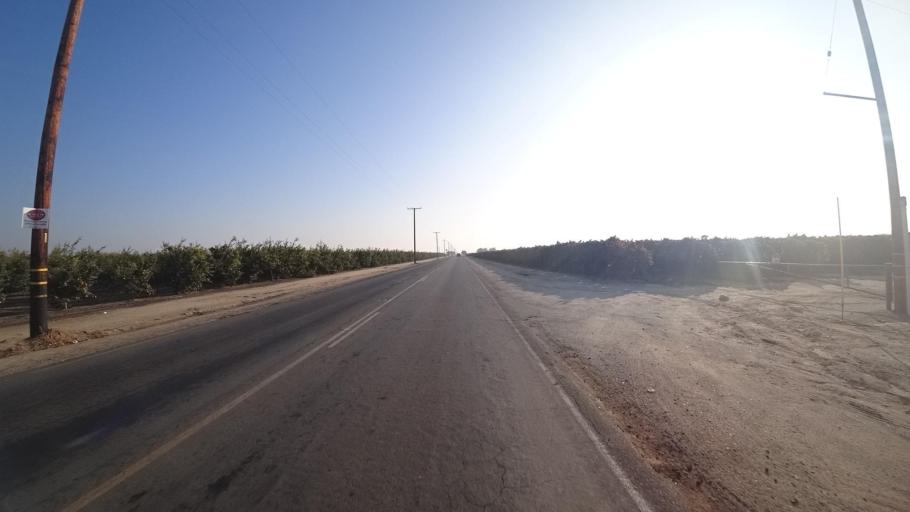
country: US
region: California
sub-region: Kern County
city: Delano
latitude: 35.7905
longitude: -119.1968
